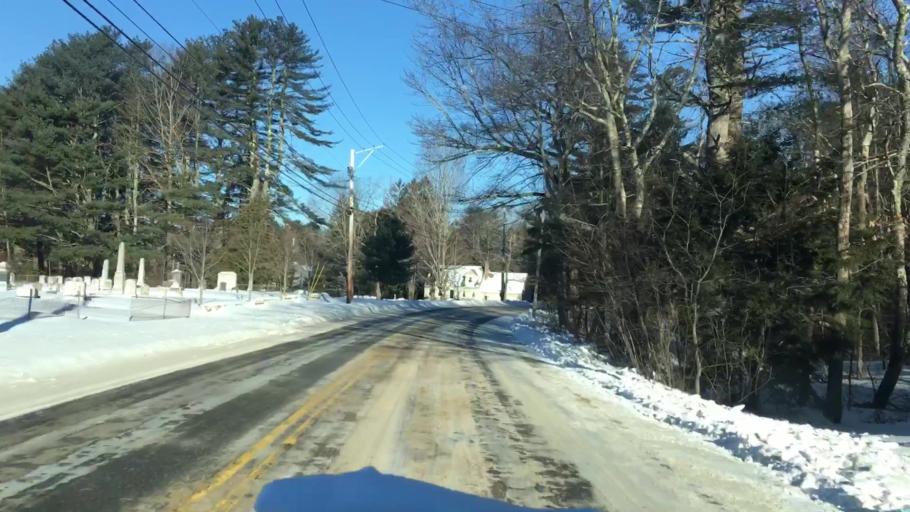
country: US
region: Maine
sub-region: Cumberland County
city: Brunswick
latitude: 43.9507
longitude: -69.9301
